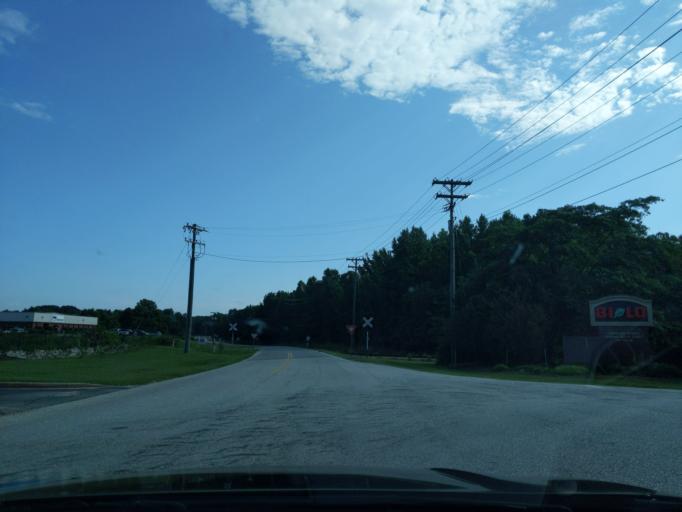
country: US
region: South Carolina
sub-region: Greenville County
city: Mauldin
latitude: 34.8025
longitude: -82.3125
